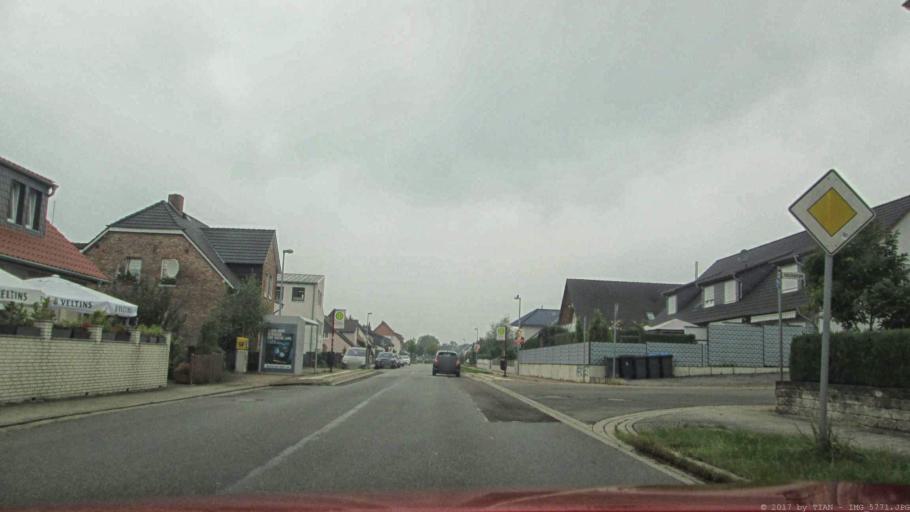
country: DE
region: Lower Saxony
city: Wolfsburg
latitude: 52.4462
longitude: 10.7801
